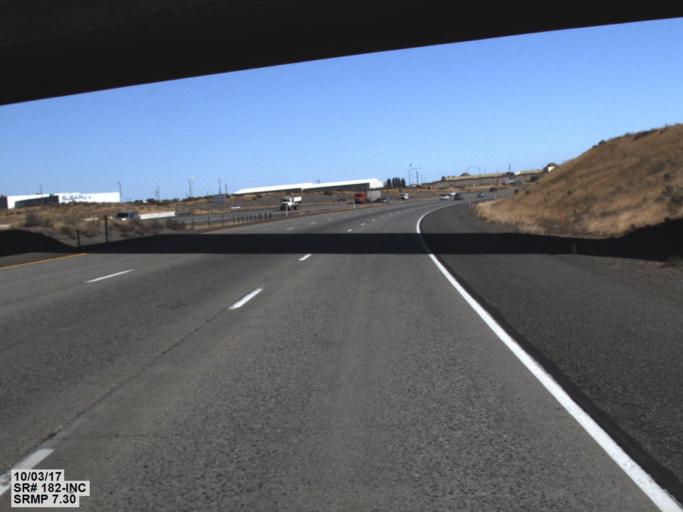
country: US
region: Washington
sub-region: Franklin County
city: West Pasco
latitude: 46.2750
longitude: -119.2217
